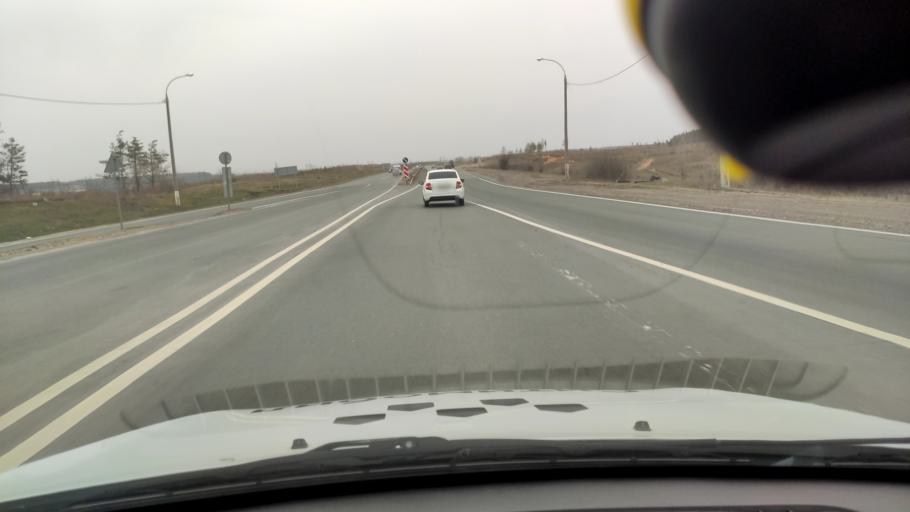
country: RU
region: Samara
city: Zhigulevsk
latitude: 53.5031
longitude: 49.5378
